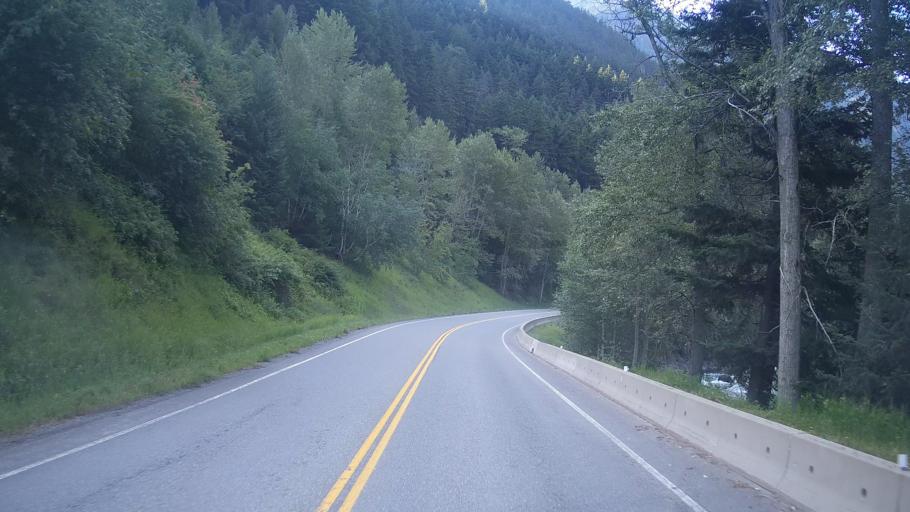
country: CA
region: British Columbia
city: Lillooet
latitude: 50.5726
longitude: -122.0881
